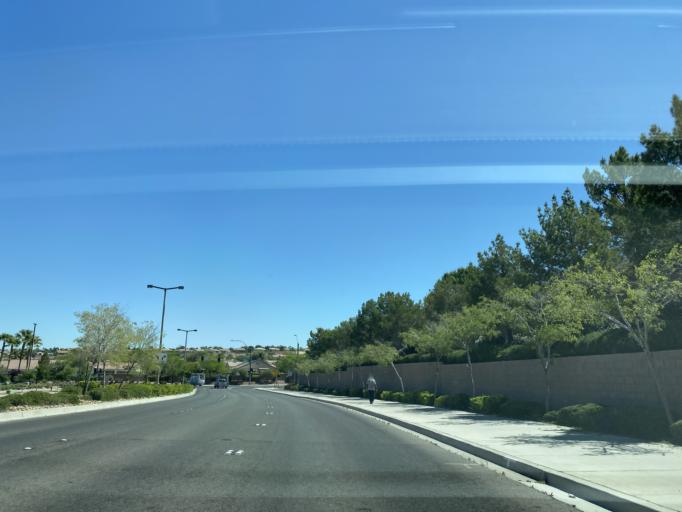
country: US
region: Nevada
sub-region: Clark County
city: Whitney
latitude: 35.9415
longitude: -115.1157
